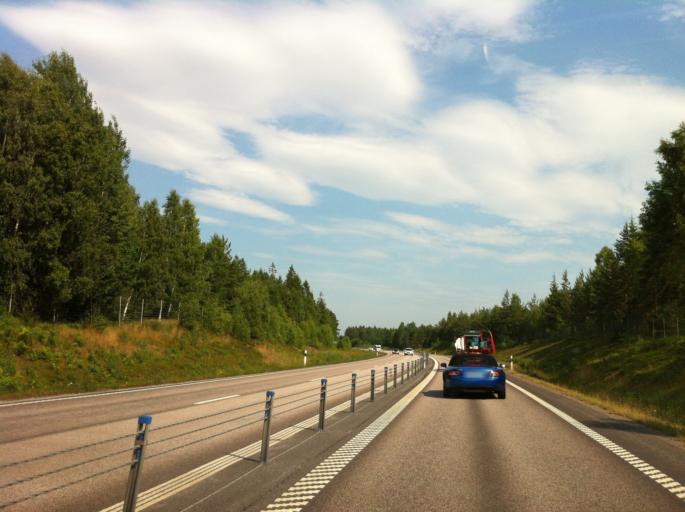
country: SE
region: Kalmar
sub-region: Kalmar Kommun
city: Trekanten
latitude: 56.6935
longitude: 16.1075
